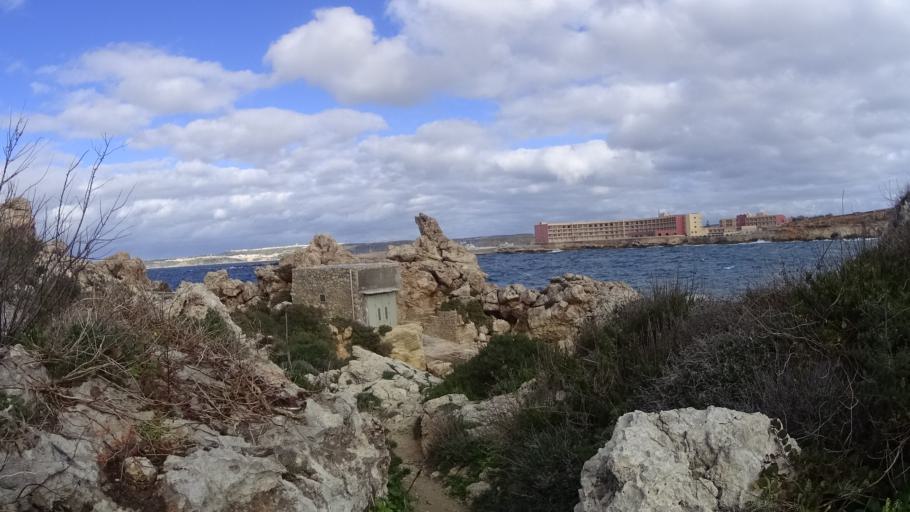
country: MT
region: Il-Mellieha
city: Mellieha
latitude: 35.9821
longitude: 14.3314
